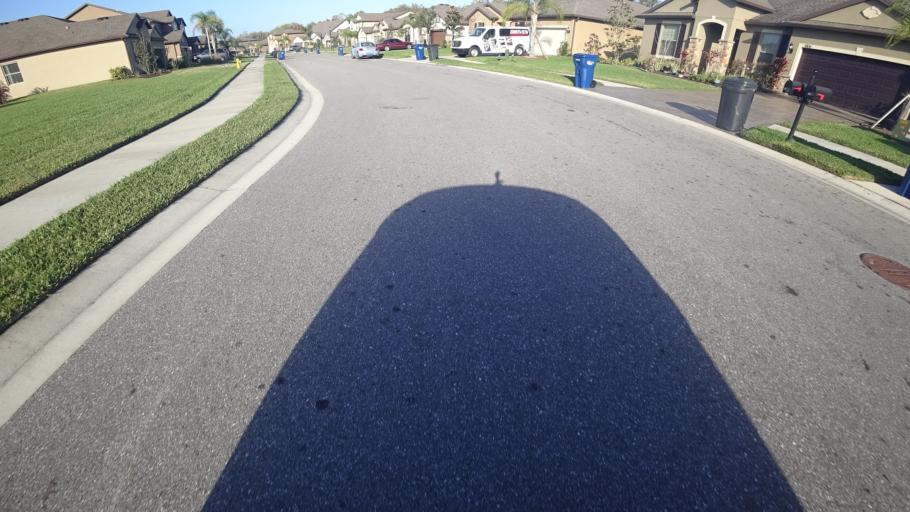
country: US
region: Florida
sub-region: Manatee County
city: Ellenton
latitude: 27.5715
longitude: -82.4475
